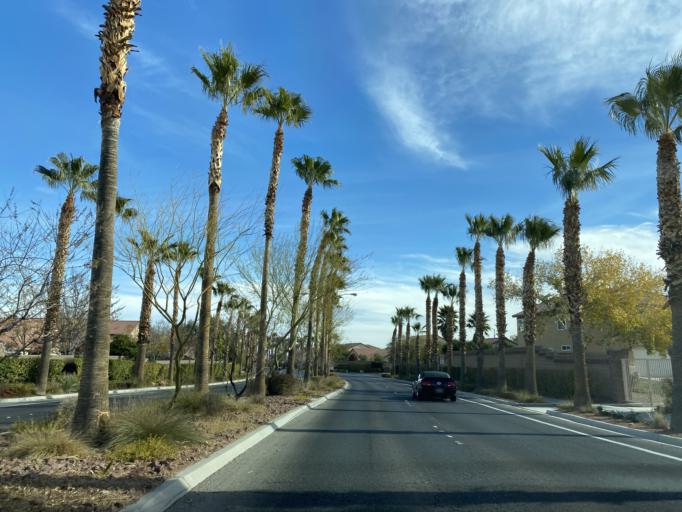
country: US
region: Nevada
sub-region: Clark County
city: Enterprise
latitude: 36.0482
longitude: -115.2545
